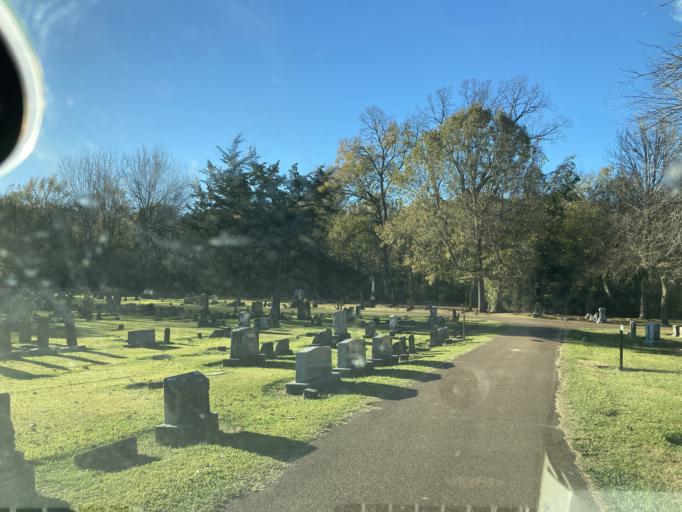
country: US
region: Mississippi
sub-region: Yazoo County
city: Yazoo City
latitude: 32.8507
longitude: -90.4013
